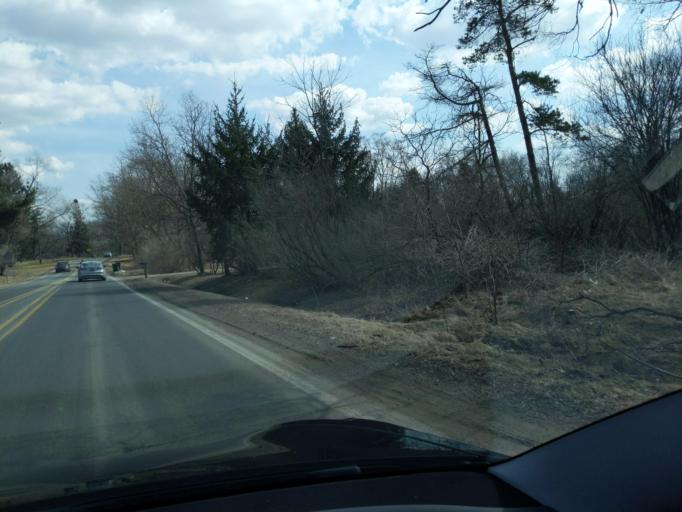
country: US
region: Michigan
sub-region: Washtenaw County
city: Dexter
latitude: 42.3875
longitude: -83.9156
